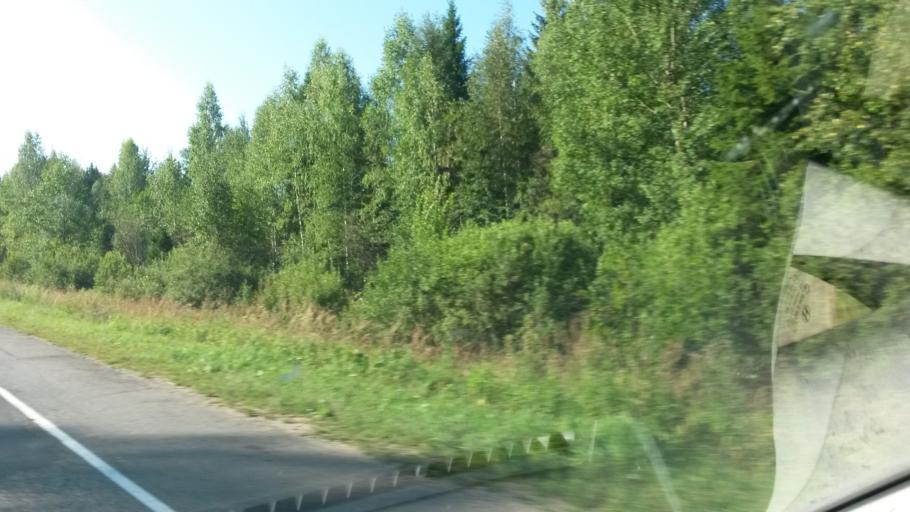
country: RU
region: Ivanovo
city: Pistsovo
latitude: 57.1031
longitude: 40.6532
